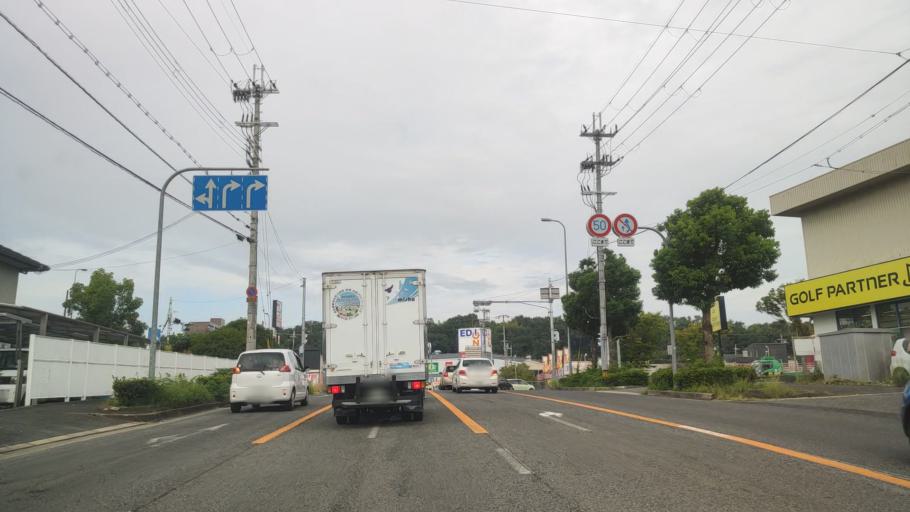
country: JP
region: Osaka
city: Tondabayashicho
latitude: 34.4444
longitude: 135.5543
